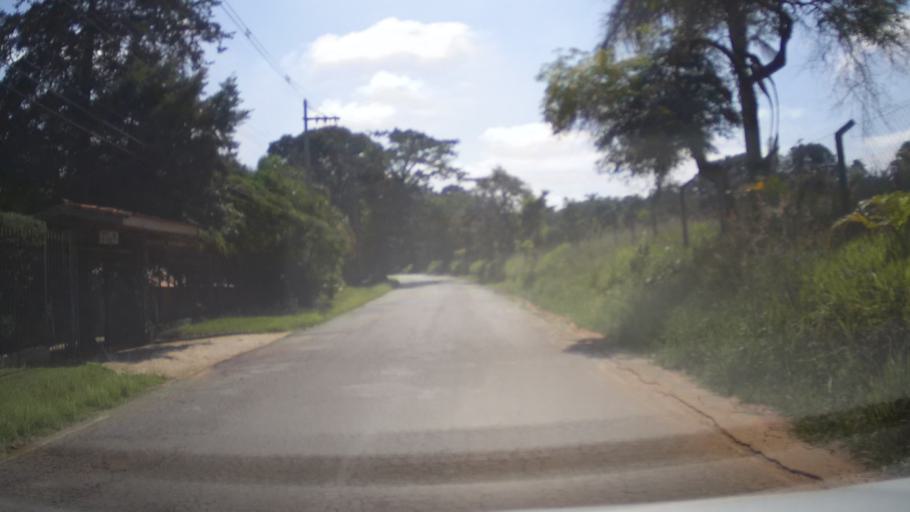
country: BR
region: Sao Paulo
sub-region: Itupeva
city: Itupeva
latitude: -23.2122
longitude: -47.0698
